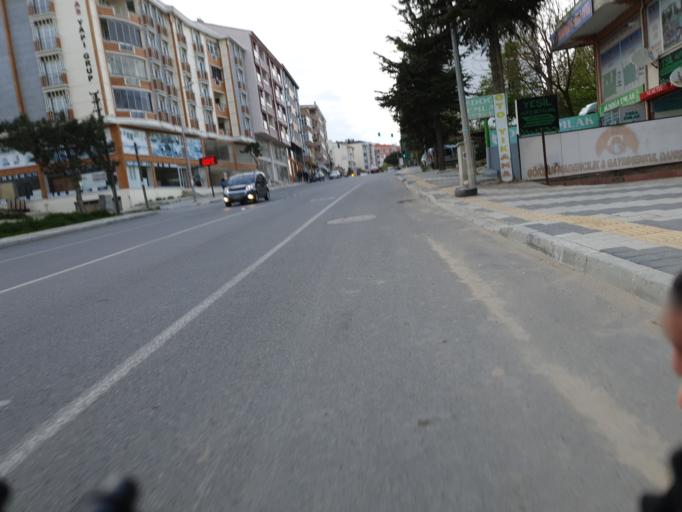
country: TR
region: Tekirdag
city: Saray
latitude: 41.4360
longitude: 27.9191
